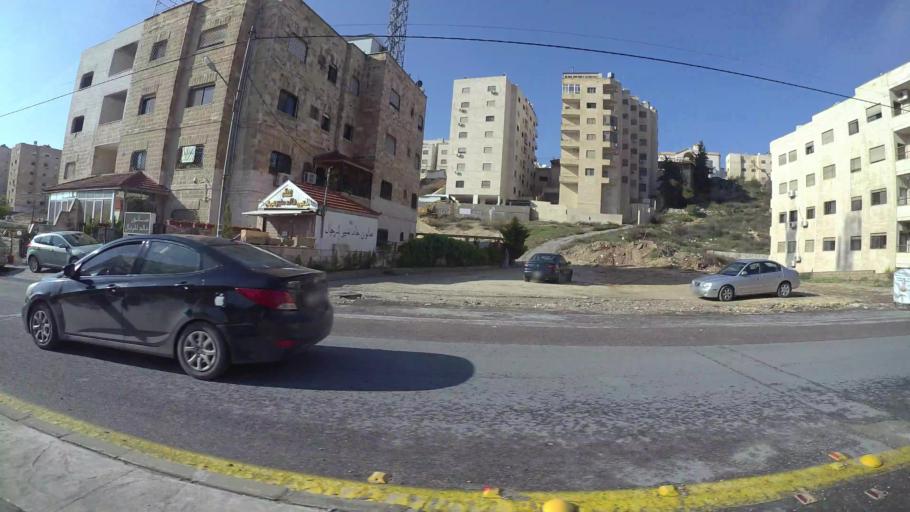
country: JO
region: Amman
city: Al Jubayhah
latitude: 32.0018
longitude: 35.8549
